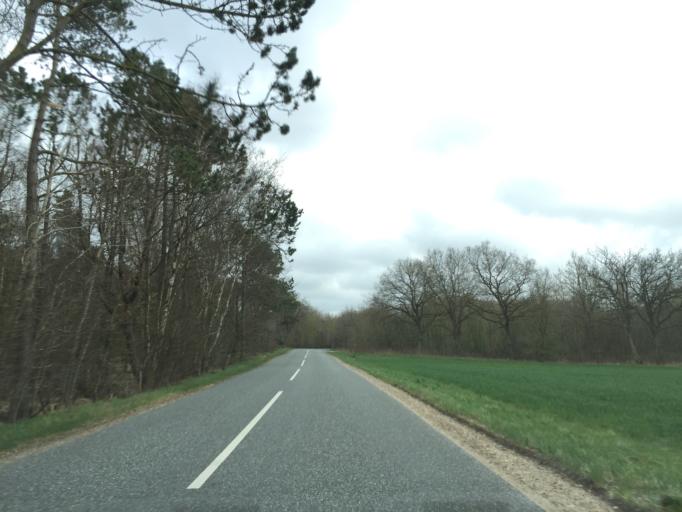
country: DK
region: Central Jutland
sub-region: Viborg Kommune
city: Bjerringbro
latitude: 56.2661
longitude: 9.6684
